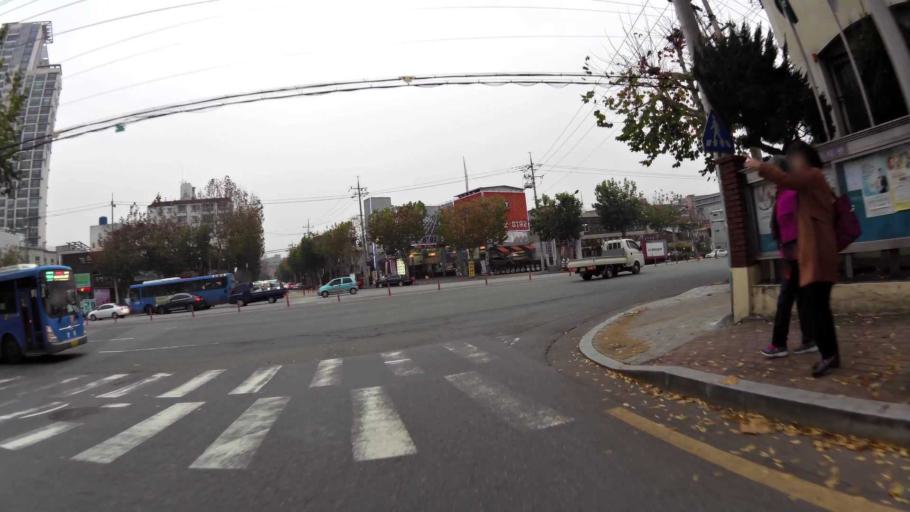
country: KR
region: Daegu
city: Daegu
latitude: 35.8597
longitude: 128.6471
